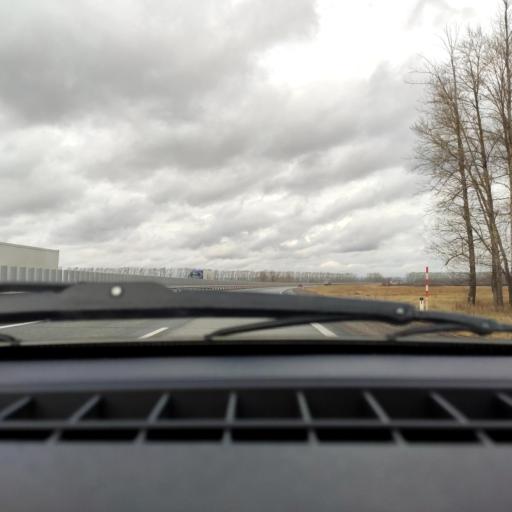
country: RU
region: Bashkortostan
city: Asanovo
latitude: 54.9264
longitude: 55.5772
